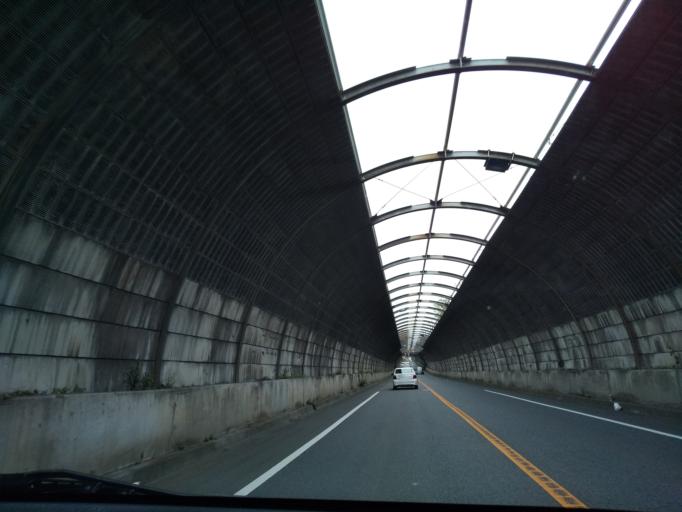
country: JP
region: Kanagawa
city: Zama
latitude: 35.5128
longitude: 139.4085
